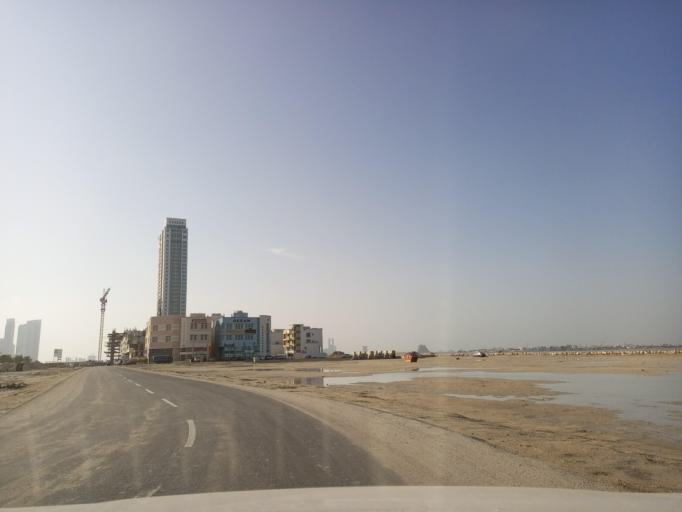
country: BH
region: Muharraq
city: Al Hadd
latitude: 26.2260
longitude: 50.6350
